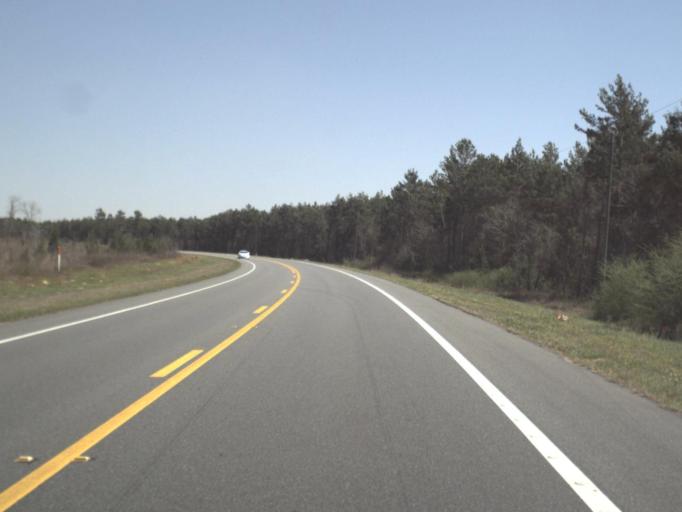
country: US
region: Florida
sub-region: Bay County
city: Youngstown
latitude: 30.4219
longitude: -85.3102
